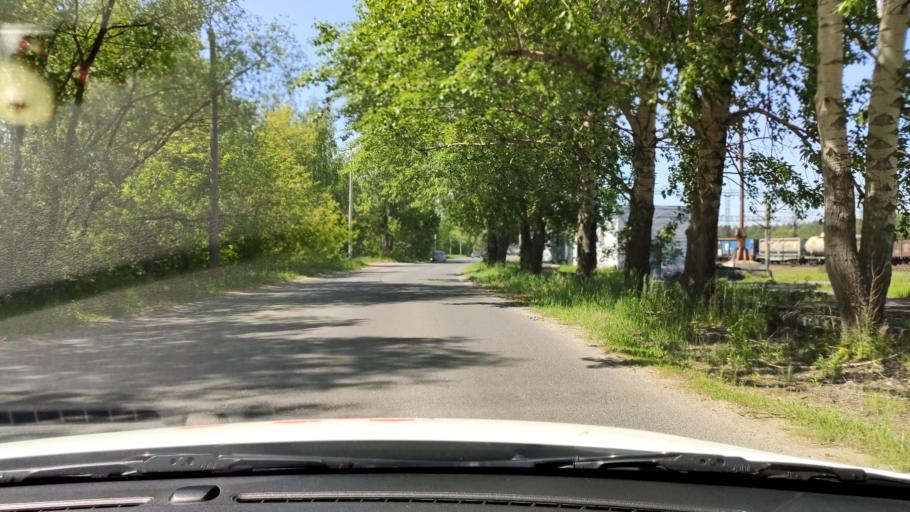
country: RU
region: Tatarstan
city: Osinovo
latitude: 55.8190
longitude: 48.8612
